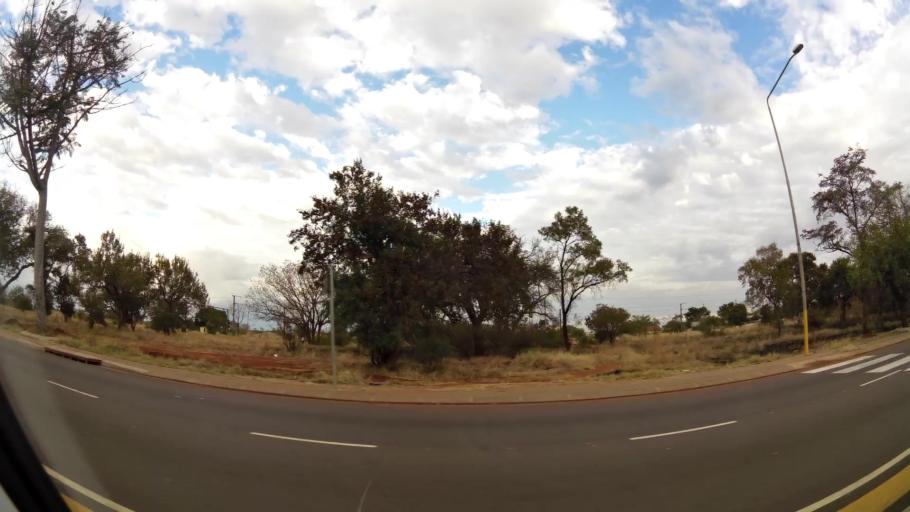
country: ZA
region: Limpopo
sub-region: Waterberg District Municipality
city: Modimolle
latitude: -24.5125
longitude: 28.7214
